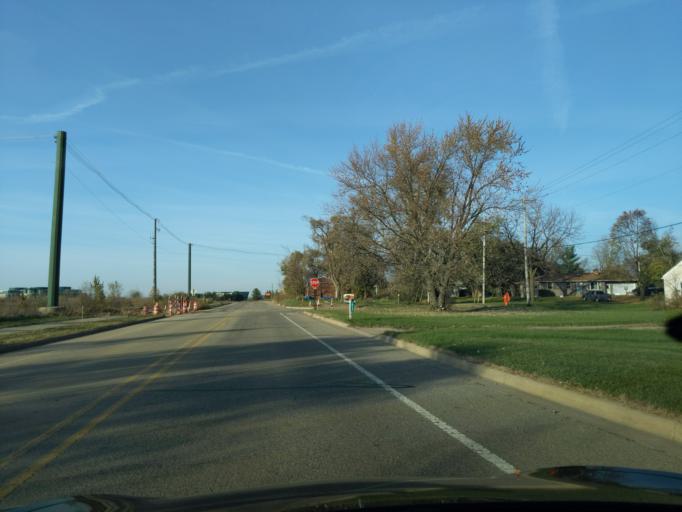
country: US
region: Michigan
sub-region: Ingham County
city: East Lansing
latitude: 42.7727
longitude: -84.5084
